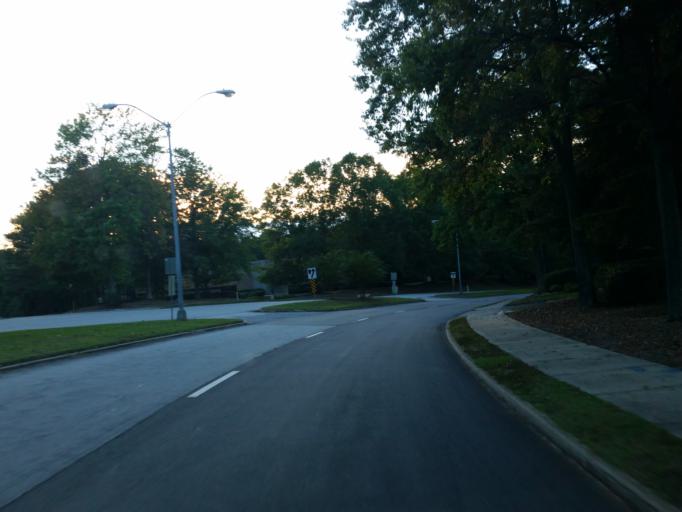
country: US
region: Georgia
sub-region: Cobb County
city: Vinings
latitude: 33.8278
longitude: -84.5066
